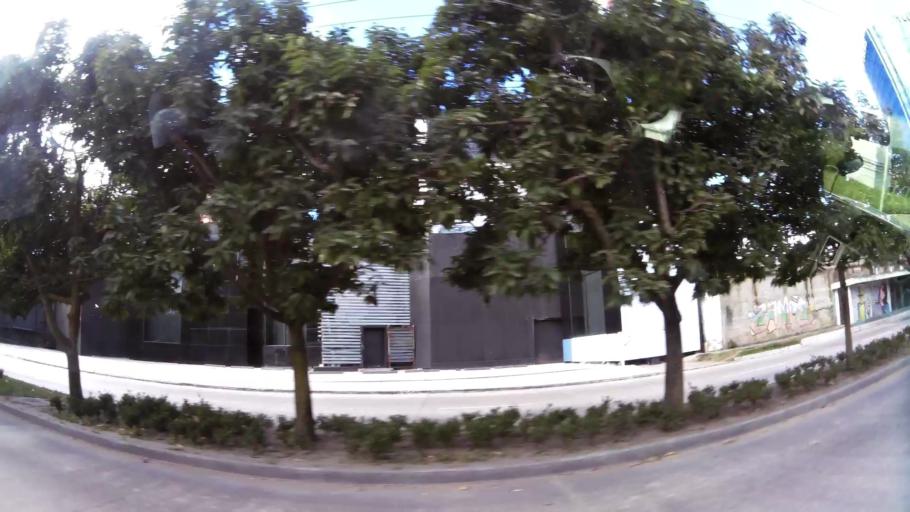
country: GT
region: Guatemala
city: Santa Catarina Pinula
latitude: 14.6008
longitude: -90.5092
